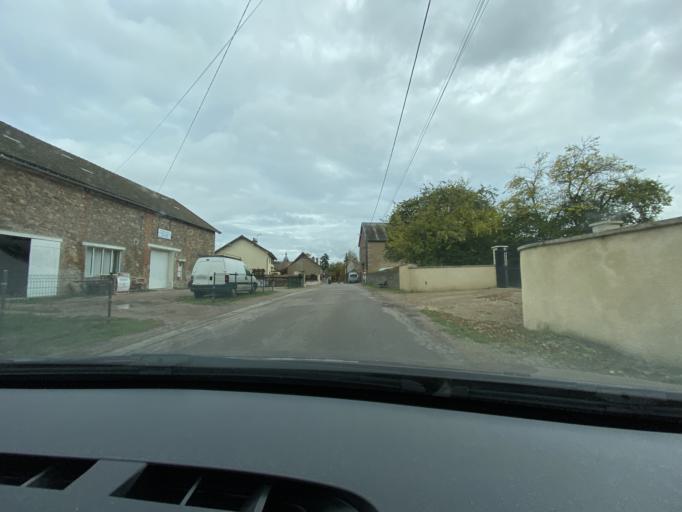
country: FR
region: Bourgogne
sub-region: Departement de la Cote-d'Or
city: Saulieu
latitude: 47.2789
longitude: 4.2246
